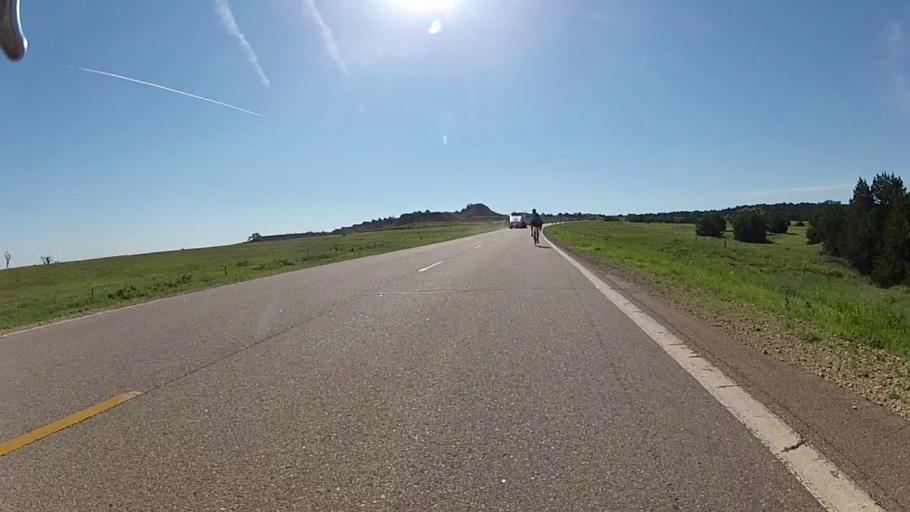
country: US
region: Kansas
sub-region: Barber County
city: Medicine Lodge
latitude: 37.2822
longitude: -98.7537
